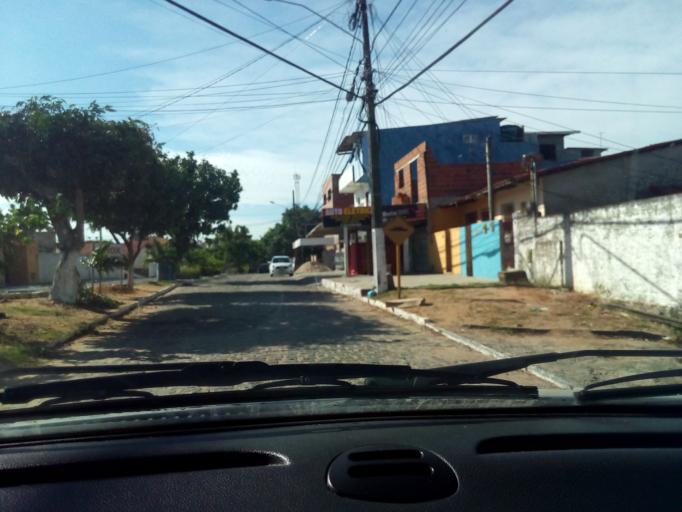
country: BR
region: Rio Grande do Norte
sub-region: Parnamirim
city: Parnamirim
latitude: -5.8849
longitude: -35.2045
